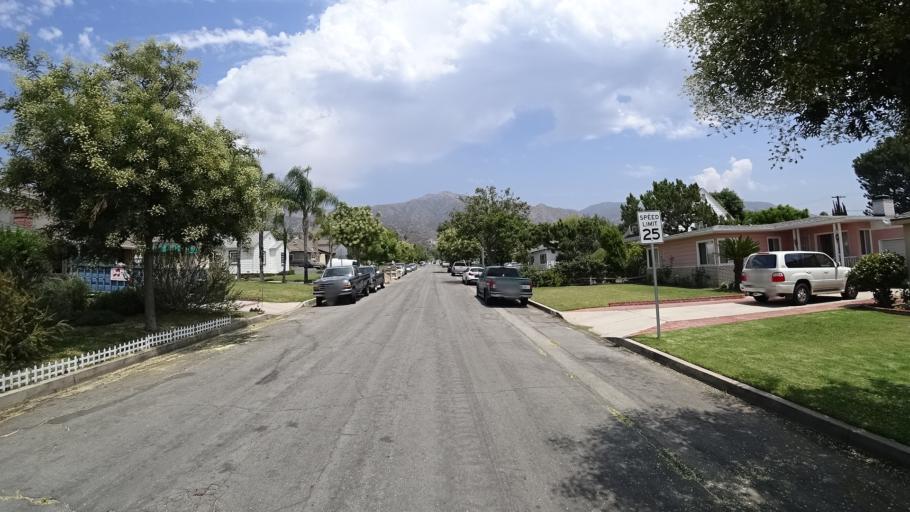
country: US
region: California
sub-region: Los Angeles County
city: Burbank
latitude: 34.1841
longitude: -118.2950
